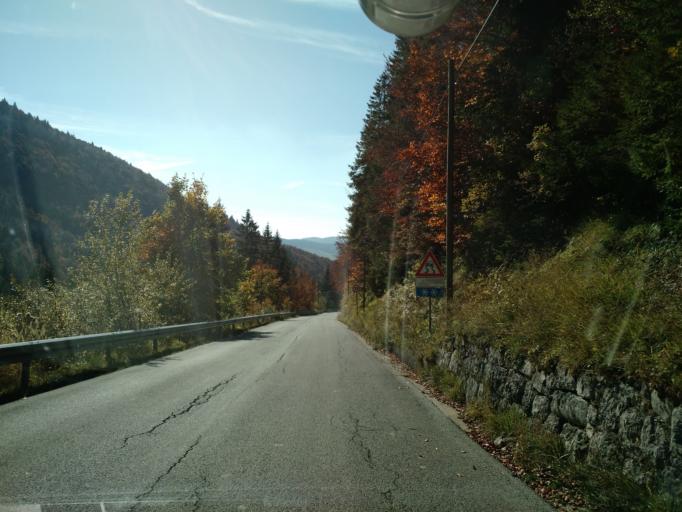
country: IT
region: Veneto
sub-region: Provincia di Vicenza
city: Gallio
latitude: 45.9093
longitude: 11.5684
